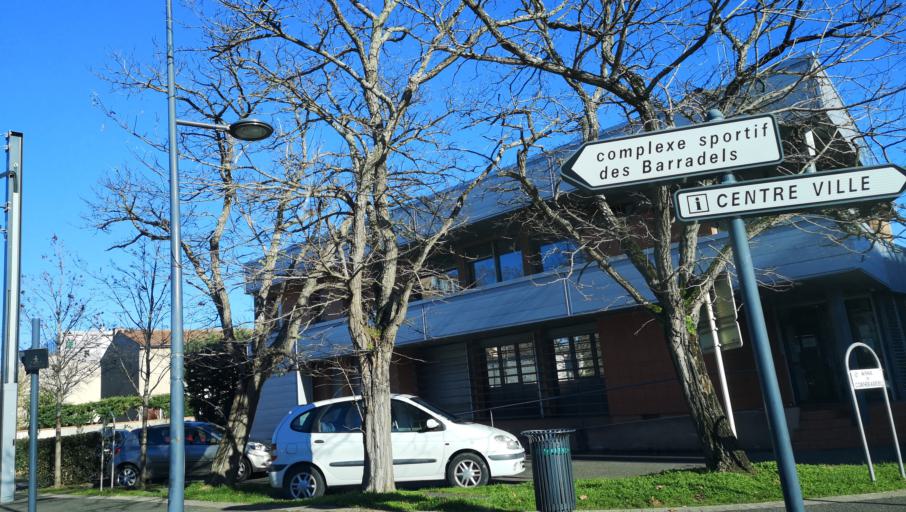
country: FR
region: Midi-Pyrenees
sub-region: Departement de la Haute-Garonne
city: Blagnac
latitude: 43.6376
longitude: 1.3837
